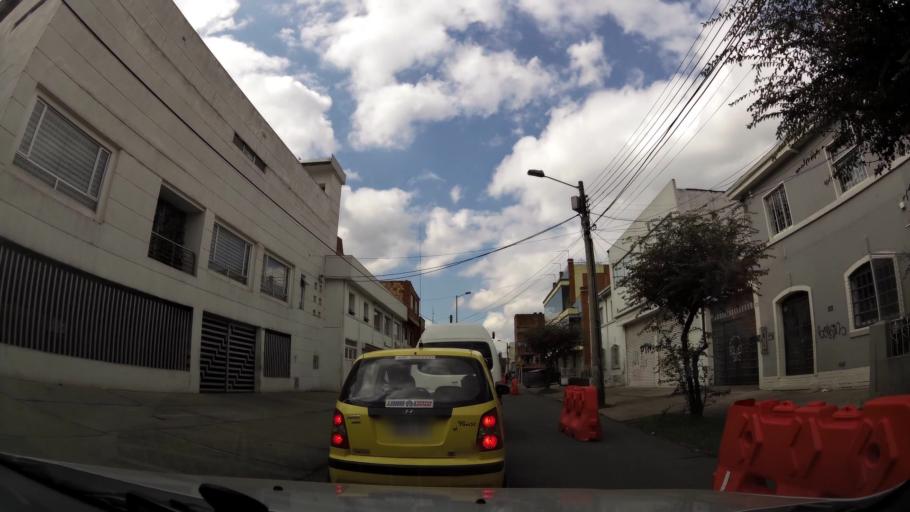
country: CO
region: Bogota D.C.
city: Bogota
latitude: 4.6417
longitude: -74.0697
